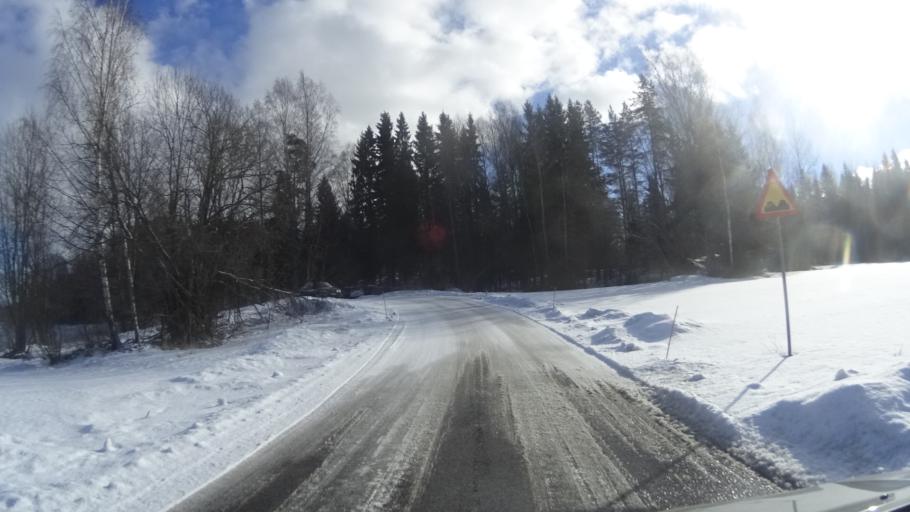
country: FI
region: Uusimaa
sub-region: Helsinki
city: Vantaa
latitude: 60.2489
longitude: 25.1646
